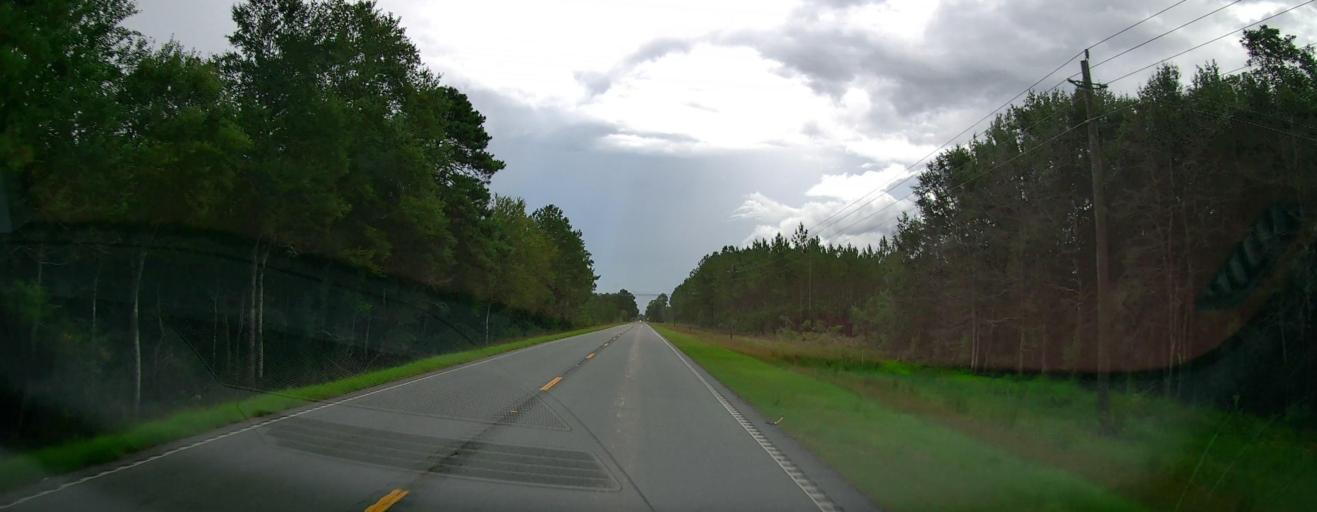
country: US
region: Georgia
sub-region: Pierce County
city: Blackshear
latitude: 31.3635
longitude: -82.0795
